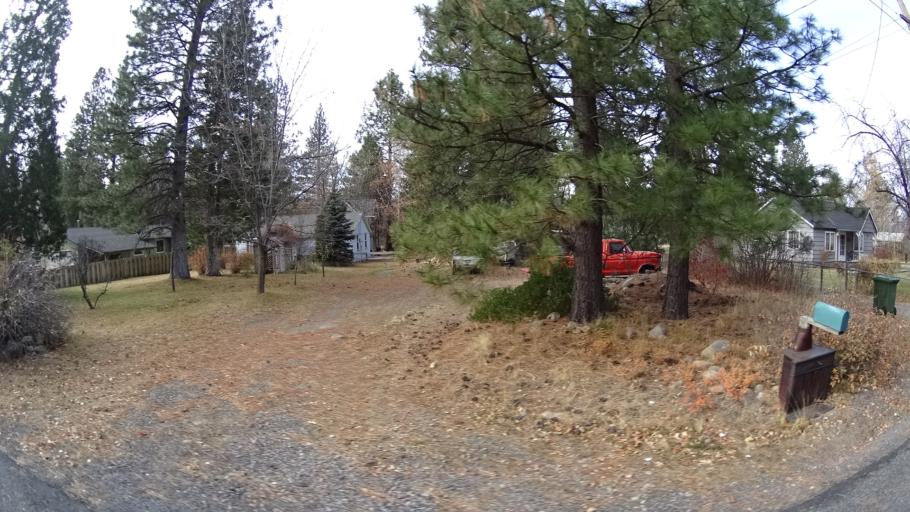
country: US
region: California
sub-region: Siskiyou County
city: Weed
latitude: 41.4465
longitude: -122.3589
